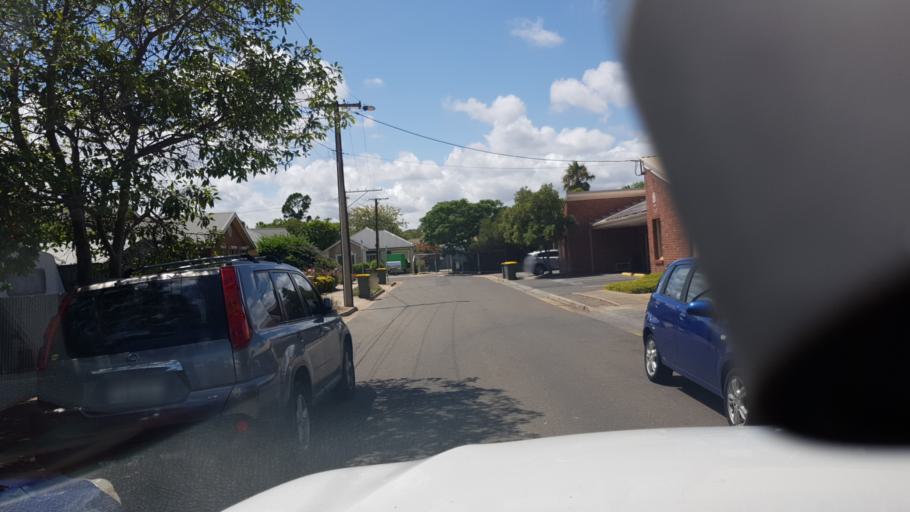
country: AU
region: South Australia
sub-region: Holdfast Bay
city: North Brighton
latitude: -35.0089
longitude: 138.5297
